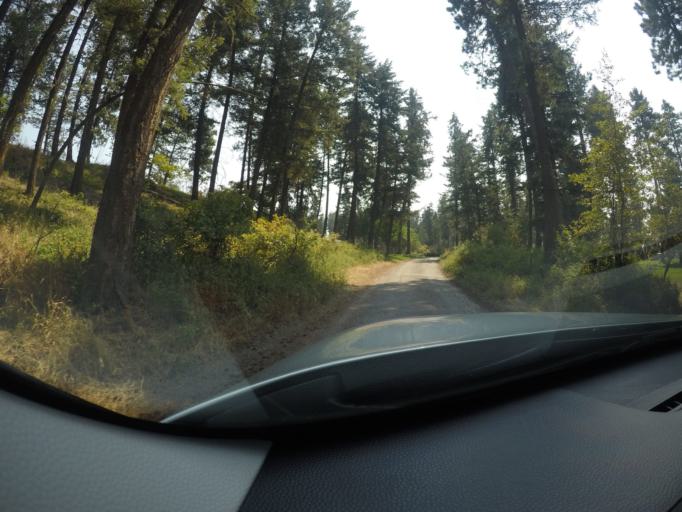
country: US
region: Montana
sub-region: Lake County
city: Polson
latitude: 47.7613
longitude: -114.1438
